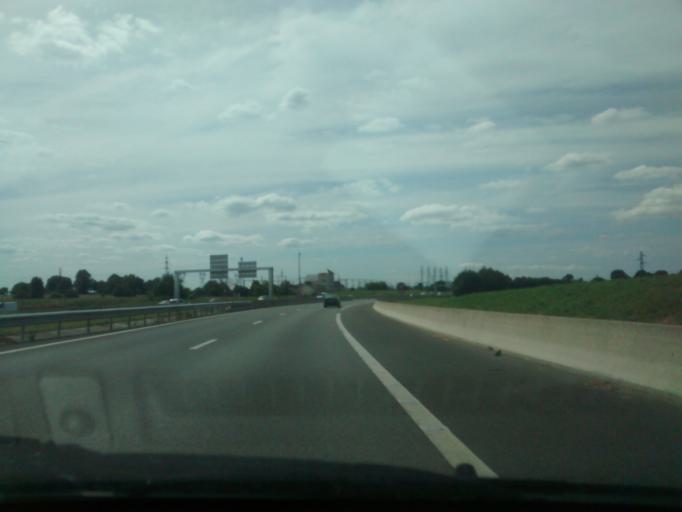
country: FR
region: Brittany
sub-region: Departement d'Ille-et-Vilaine
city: Vezin-le-Coquet
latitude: 48.1273
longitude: -1.7439
